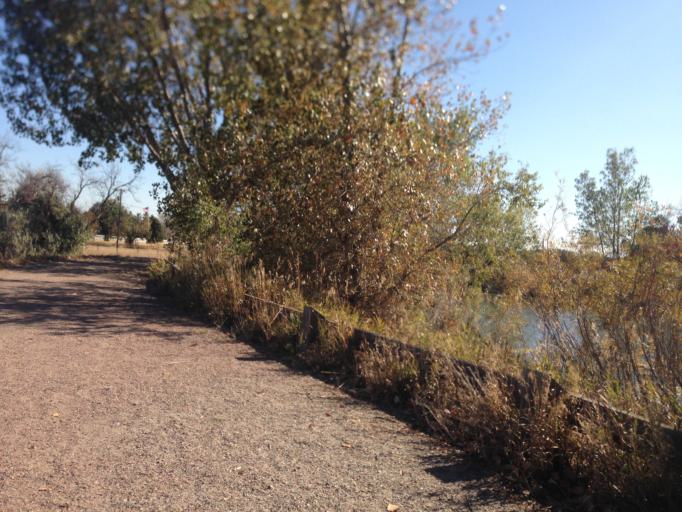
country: US
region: Colorado
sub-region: Boulder County
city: Louisville
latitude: 39.9697
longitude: -105.1434
